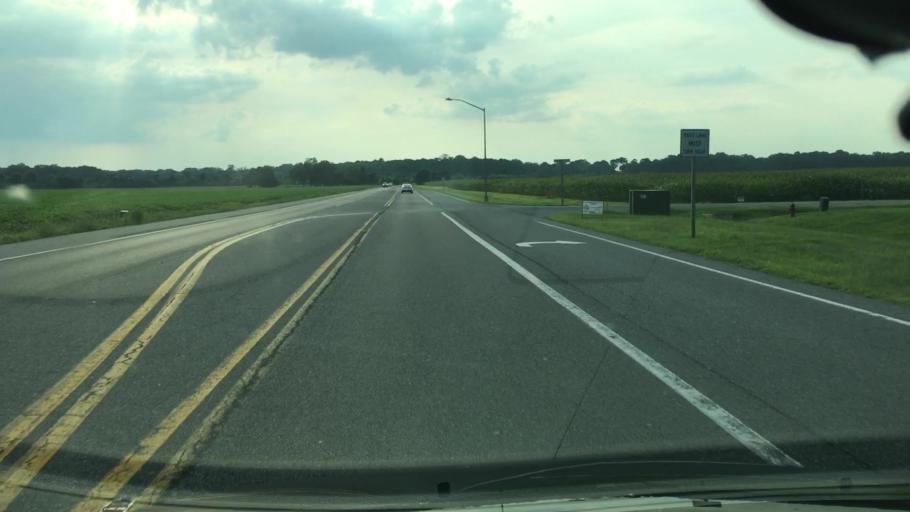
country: US
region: Maryland
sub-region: Worcester County
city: Ocean Pines
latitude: 38.3896
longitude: -75.1937
